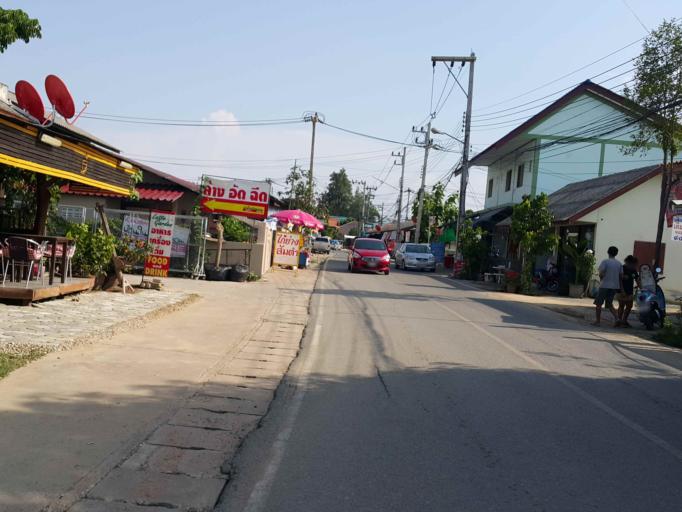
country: TH
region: Chiang Mai
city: San Sai
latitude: 18.8244
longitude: 99.0208
